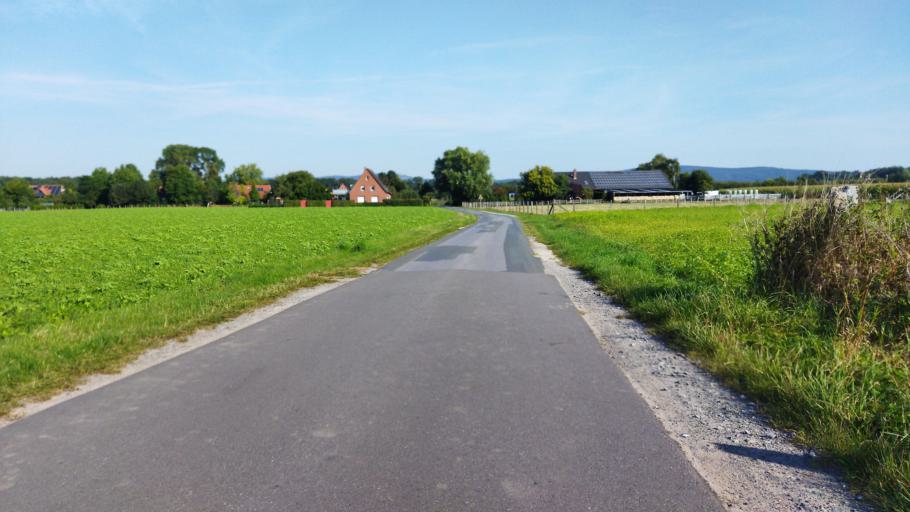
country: DE
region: Lower Saxony
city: Bad Laer
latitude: 52.1119
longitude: 8.0764
